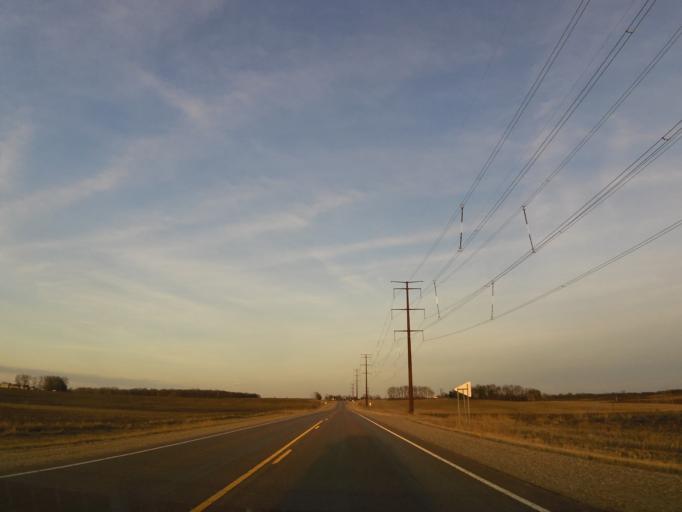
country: US
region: Minnesota
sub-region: Scott County
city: Belle Plaine
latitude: 44.6516
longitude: -93.8570
